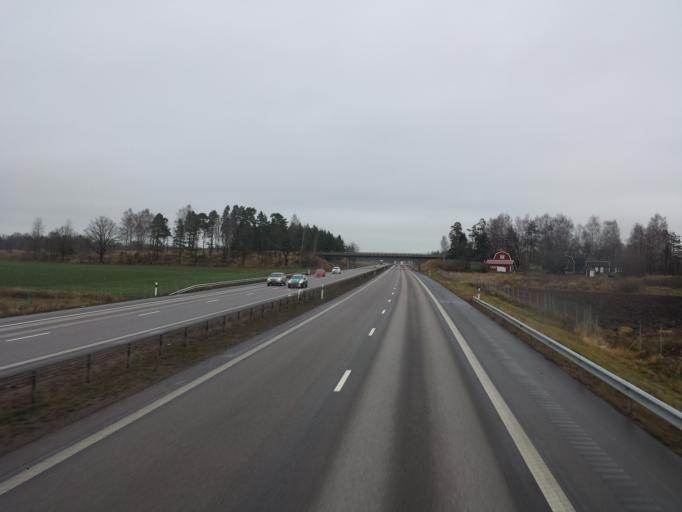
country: SE
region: OEstergoetland
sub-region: Linkopings Kommun
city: Linghem
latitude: 58.4402
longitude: 15.7103
